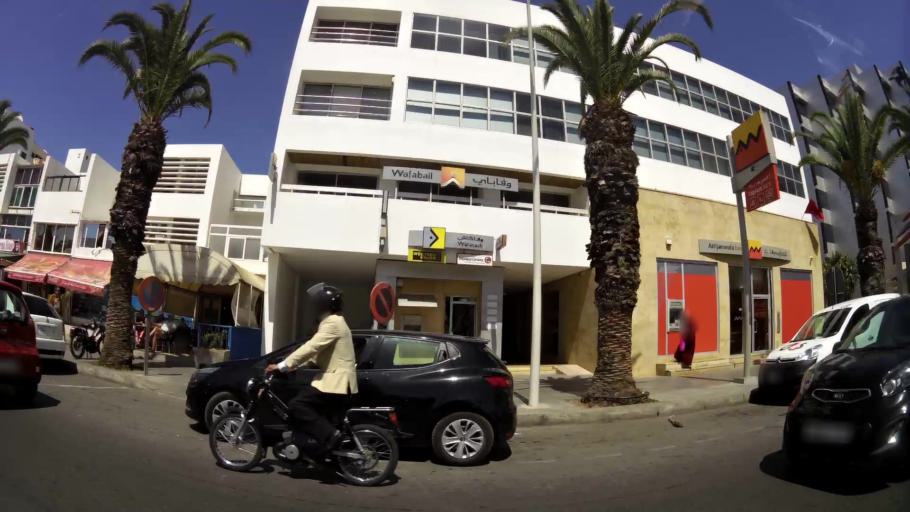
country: MA
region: Souss-Massa-Draa
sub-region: Agadir-Ida-ou-Tnan
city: Agadir
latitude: 30.4166
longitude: -9.5956
